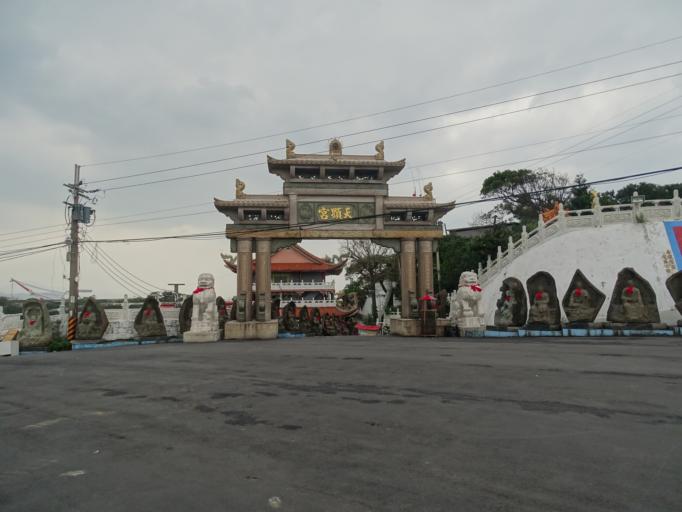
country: TW
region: Taiwan
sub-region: Keelung
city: Keelung
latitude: 25.1578
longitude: 121.7677
